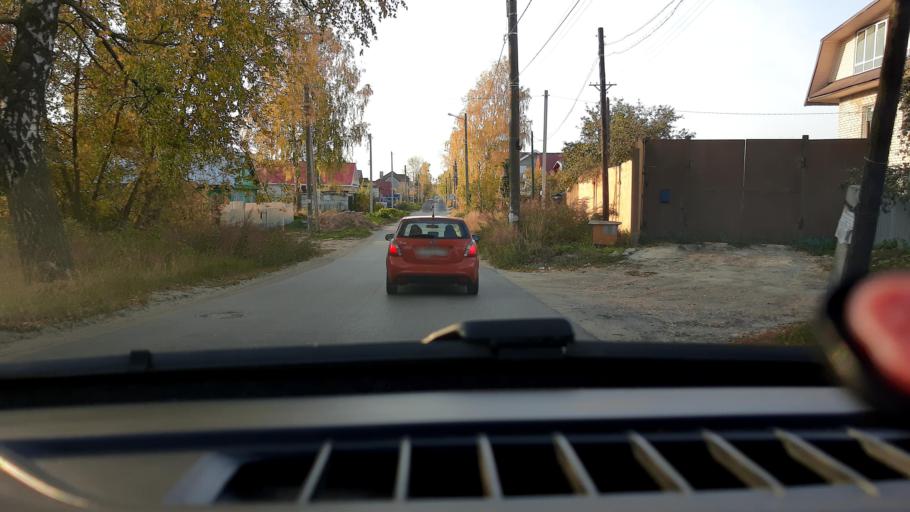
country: RU
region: Nizjnij Novgorod
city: Gorbatovka
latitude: 56.3369
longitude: 43.8305
